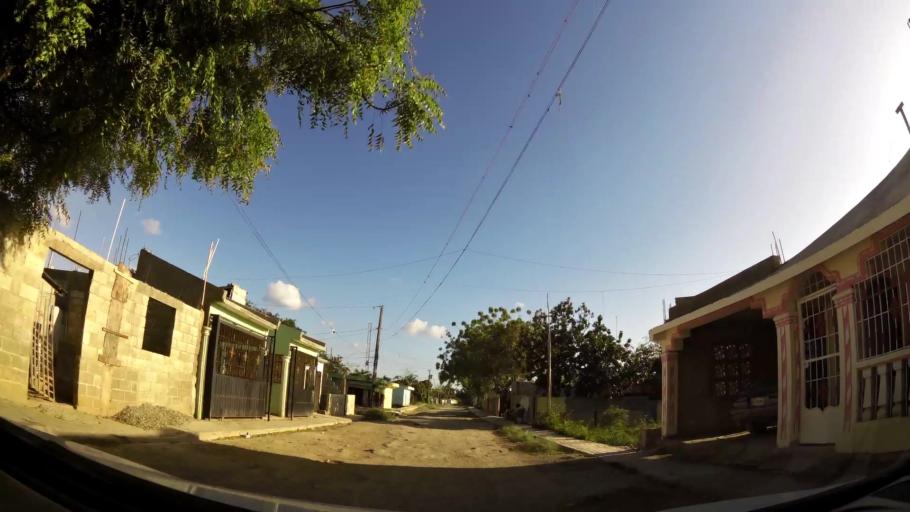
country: DO
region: Santo Domingo
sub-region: Santo Domingo
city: Santo Domingo Este
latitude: 18.4781
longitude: -69.7995
